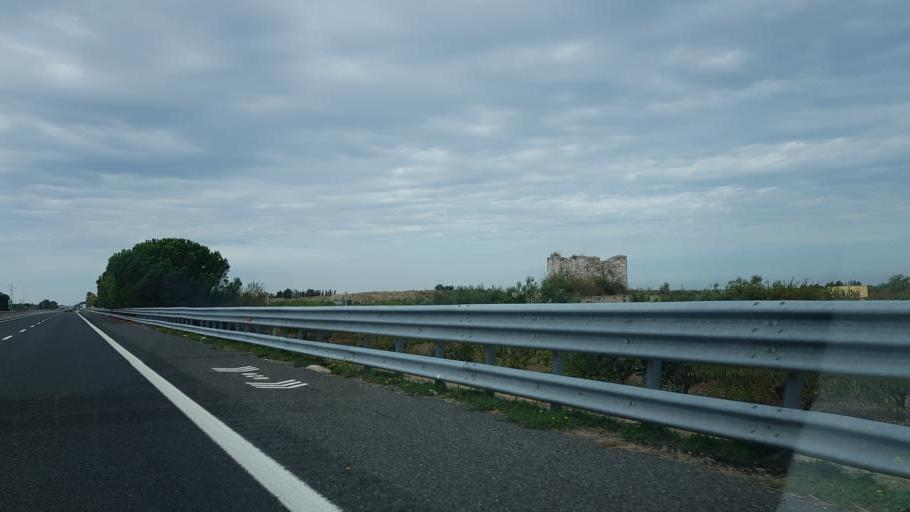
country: IT
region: Apulia
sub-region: Provincia di Barletta - Andria - Trani
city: Bisceglie
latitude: 41.1897
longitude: 16.5012
